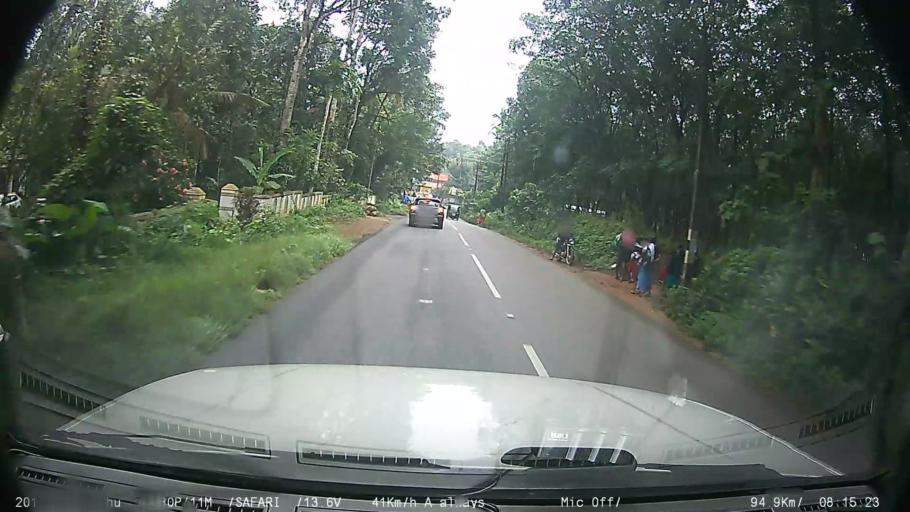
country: IN
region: Kerala
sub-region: Kottayam
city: Kottayam
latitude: 9.6296
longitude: 76.6052
